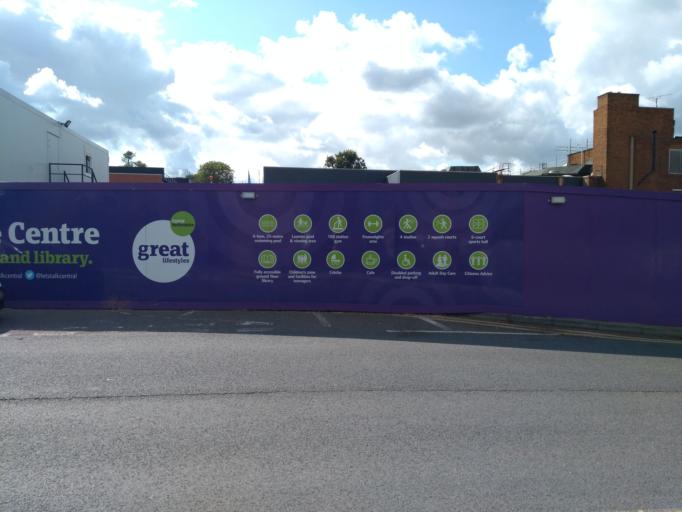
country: GB
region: England
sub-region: Central Bedfordshire
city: Dunstable
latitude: 51.8906
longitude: -0.5203
